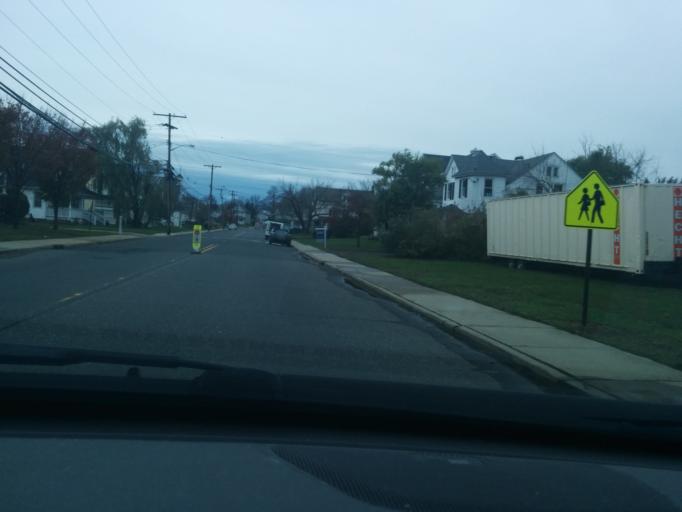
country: US
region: New Jersey
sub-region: Monmouth County
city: Monmouth Beach
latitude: 40.3294
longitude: -73.9810
